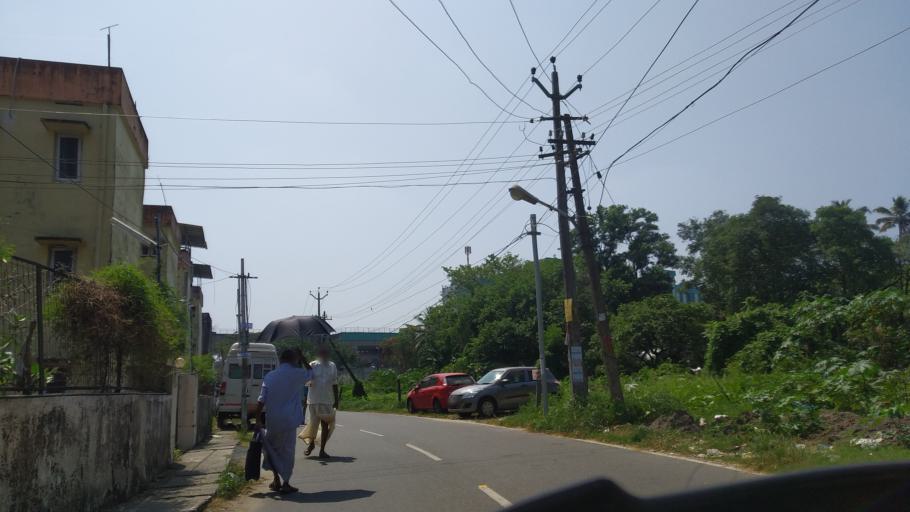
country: IN
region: Kerala
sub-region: Ernakulam
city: Elur
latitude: 10.0025
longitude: 76.2996
